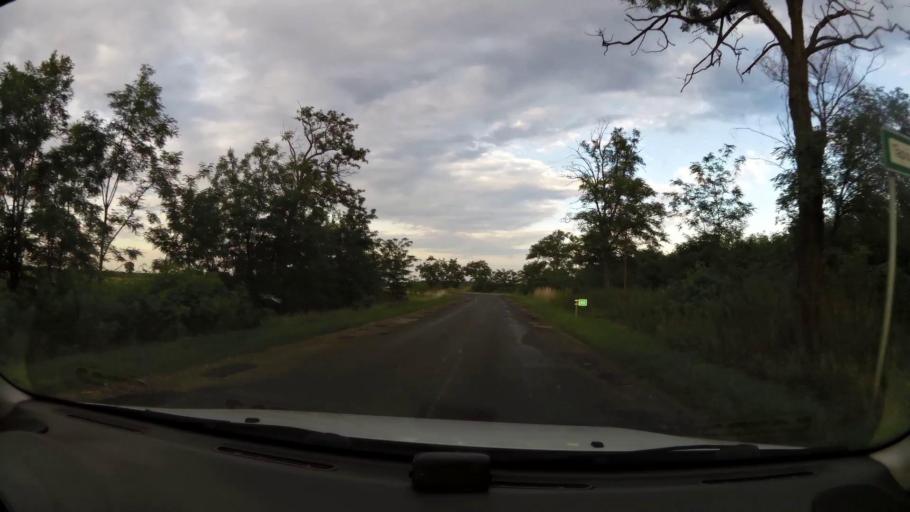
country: HU
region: Pest
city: Tapioszolos
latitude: 47.3193
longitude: 19.8493
